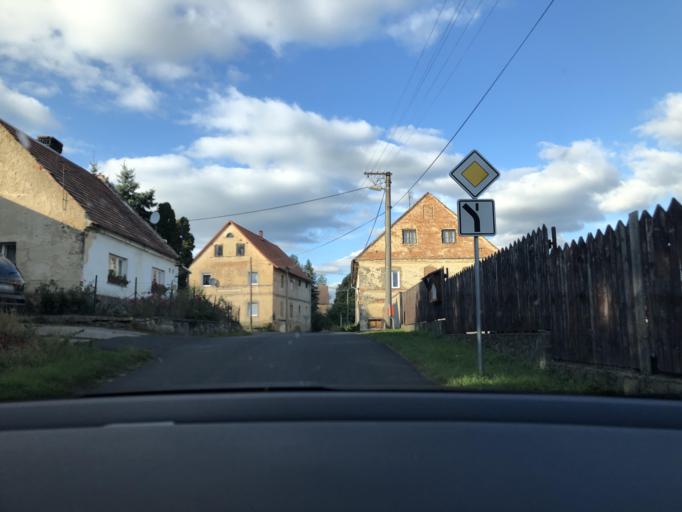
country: CZ
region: Ustecky
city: Zitenice
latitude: 50.5721
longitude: 14.1834
